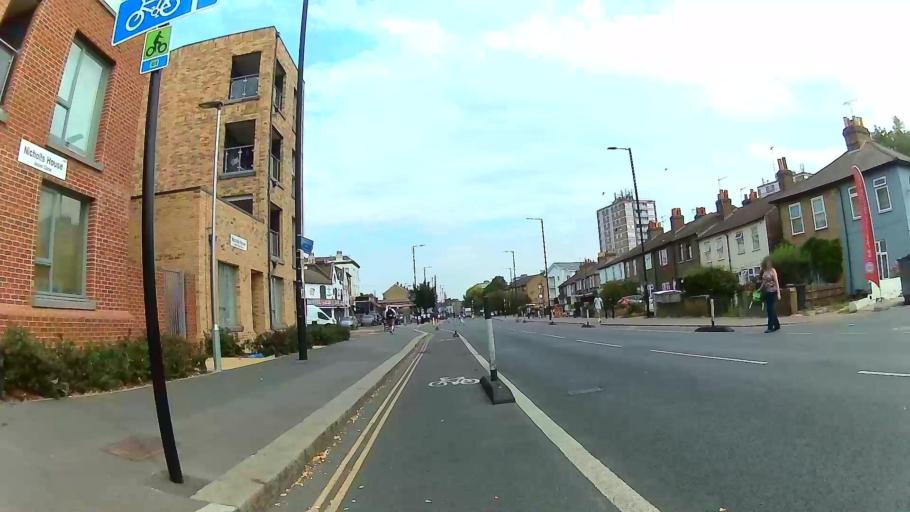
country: GB
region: England
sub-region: Hertfordshire
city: Waltham Cross
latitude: 51.6660
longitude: -0.0433
